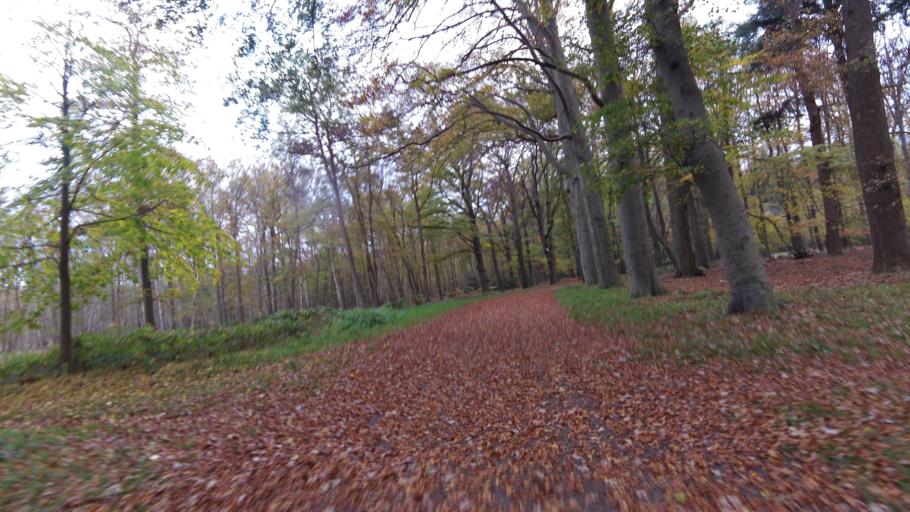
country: NL
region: North Holland
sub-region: Gemeente Hilversum
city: Hilversum
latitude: 52.2039
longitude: 5.2048
